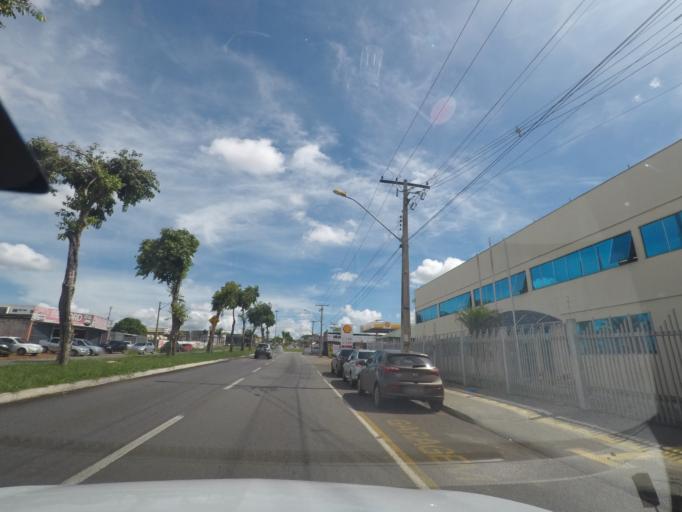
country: BR
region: Goias
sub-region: Goiania
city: Goiania
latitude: -16.7426
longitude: -49.3294
